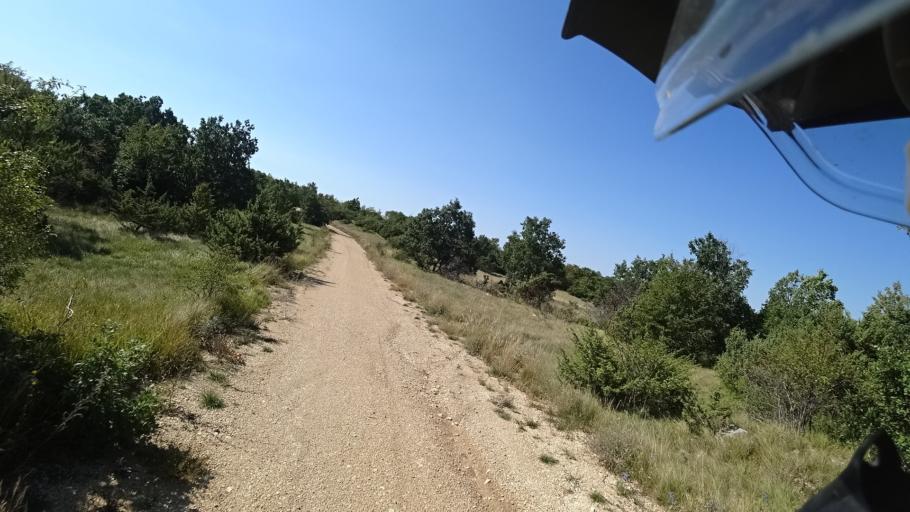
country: HR
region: Sibensko-Kniniska
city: Drnis
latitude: 43.9008
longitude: 16.1752
